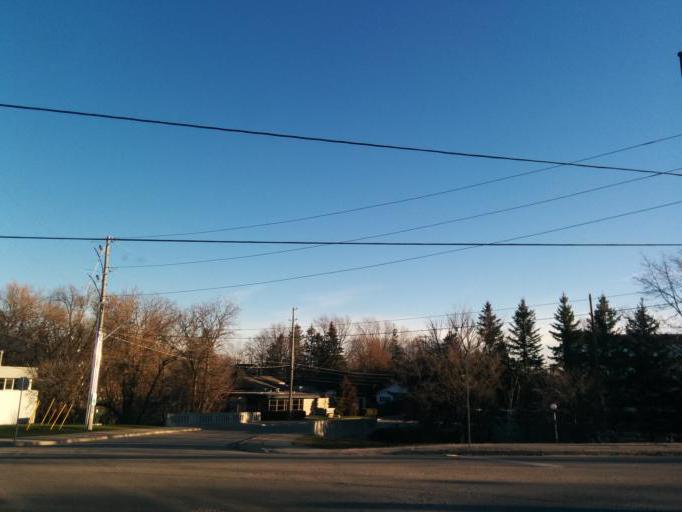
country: CA
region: Ontario
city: Orangeville
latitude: 43.9184
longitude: -80.0955
